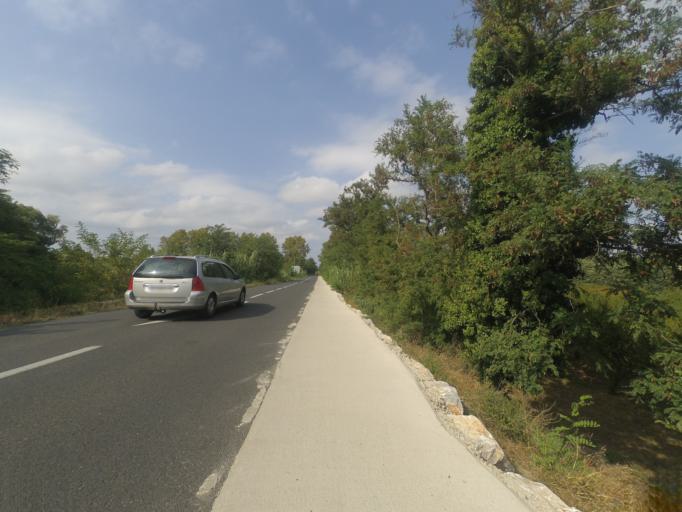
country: FR
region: Languedoc-Roussillon
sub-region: Departement des Pyrenees-Orientales
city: Le Soler
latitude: 42.6866
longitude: 2.7902
